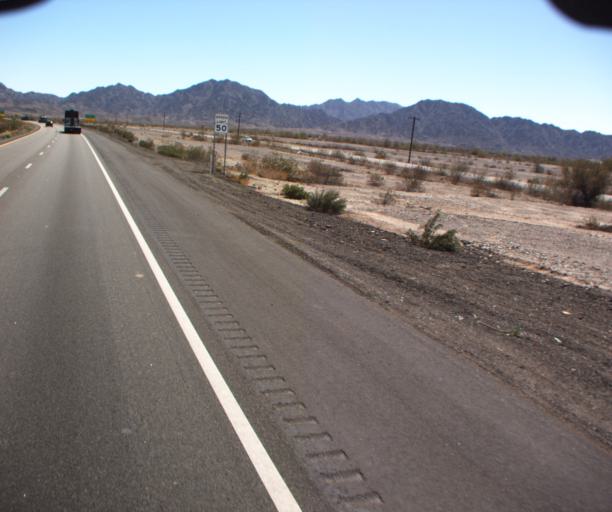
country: US
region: Arizona
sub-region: Yuma County
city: Fortuna Foothills
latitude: 32.6619
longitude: -114.3804
